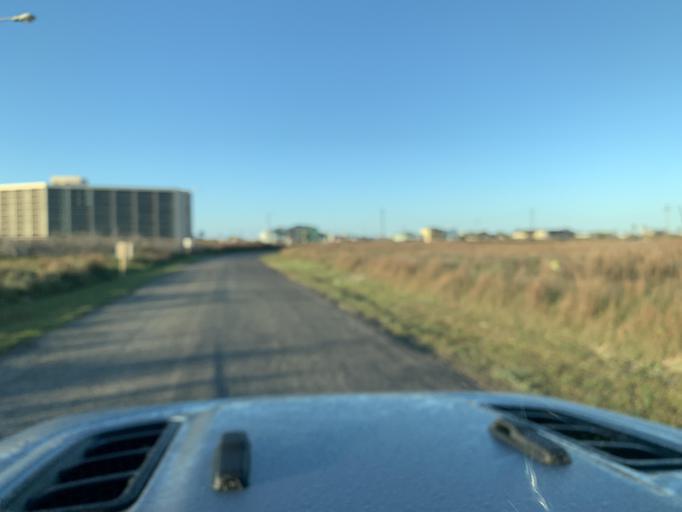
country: US
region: Texas
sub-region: Nueces County
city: Port Aransas
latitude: 27.8300
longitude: -97.0534
